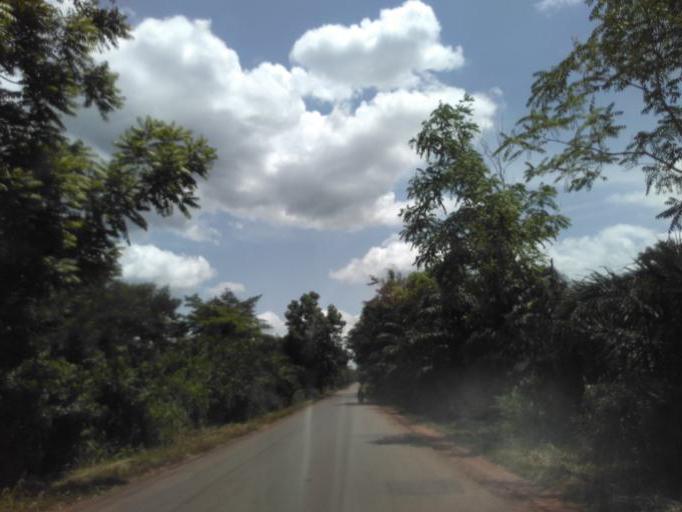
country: GH
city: Akropong
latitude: 6.1100
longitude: -0.1130
